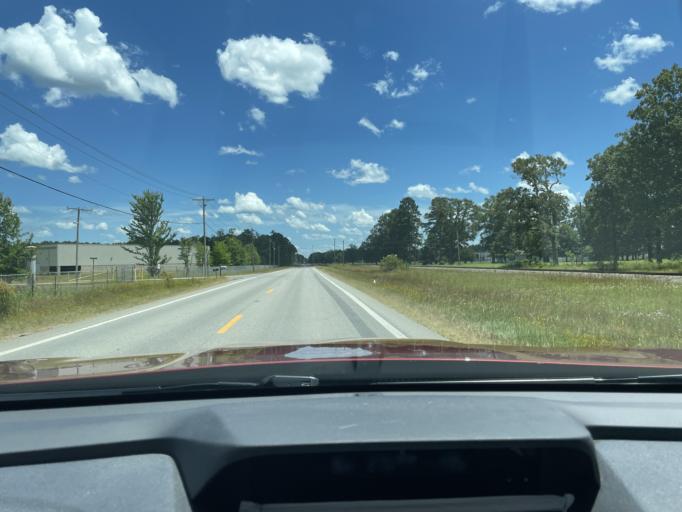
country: US
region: Arkansas
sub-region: Drew County
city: Monticello
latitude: 33.6190
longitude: -91.7475
